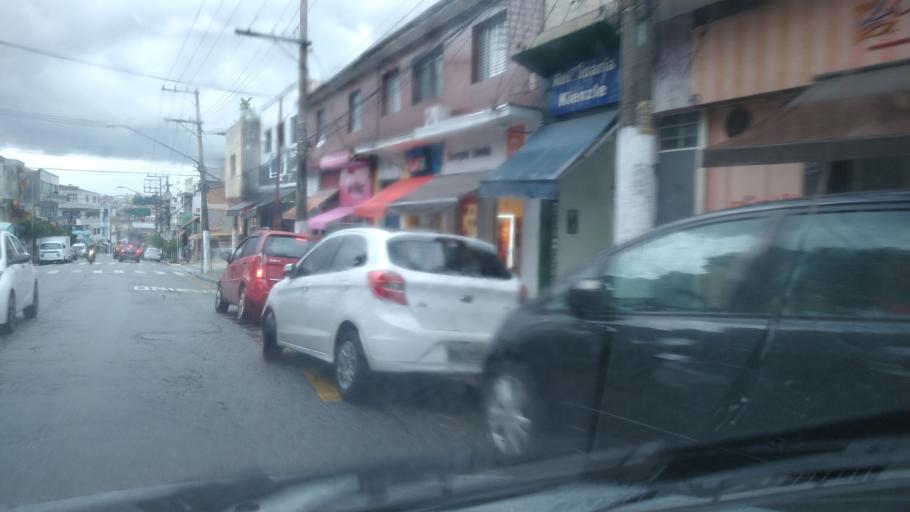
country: BR
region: Sao Paulo
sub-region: Sao Caetano Do Sul
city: Sao Caetano do Sul
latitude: -23.5941
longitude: -46.5469
